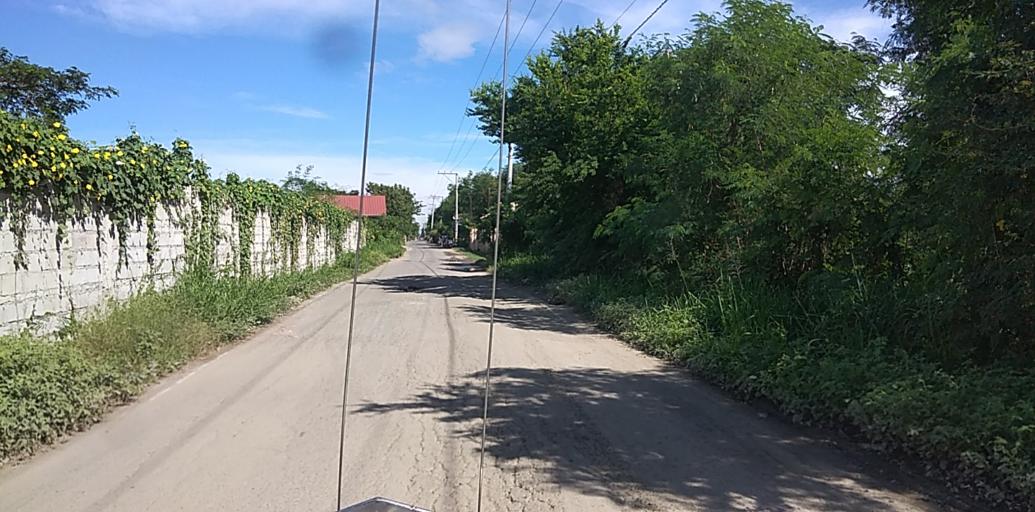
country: PH
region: Central Luzon
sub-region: Province of Pampanga
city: Candaba
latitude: 15.0776
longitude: 120.8080
